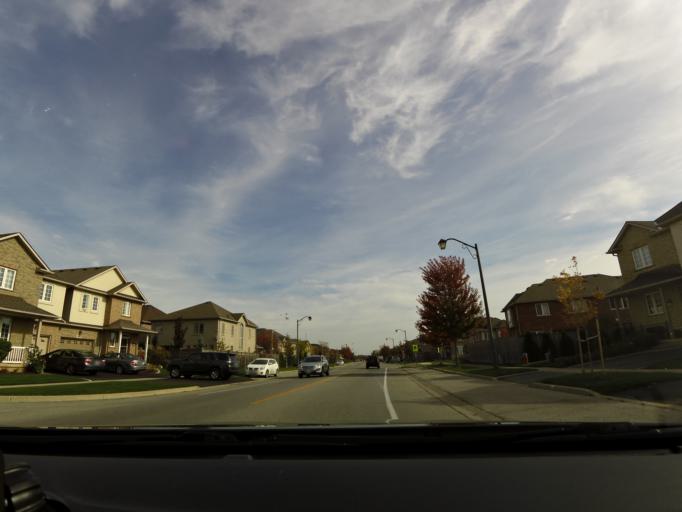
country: CA
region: Ontario
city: Burlington
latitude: 43.4108
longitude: -79.7993
